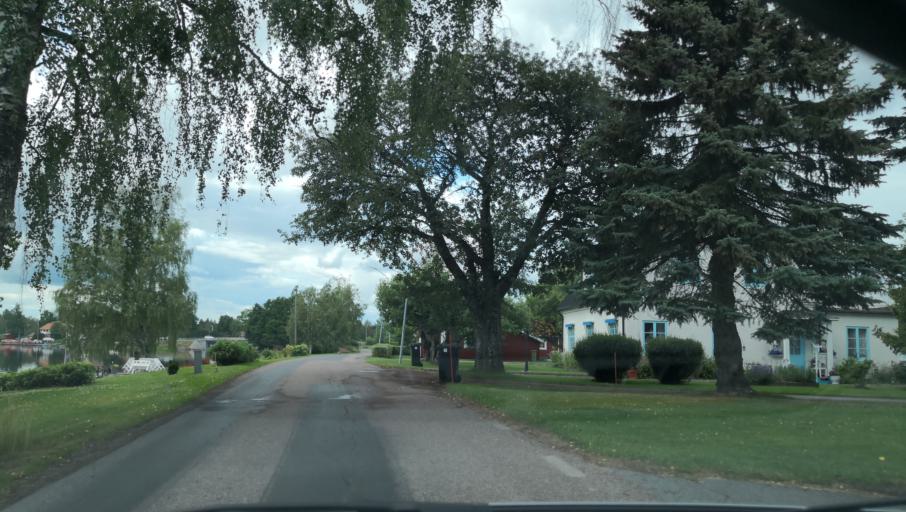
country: SE
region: Dalarna
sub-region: Borlange Kommun
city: Ornas
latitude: 60.4612
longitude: 15.5756
